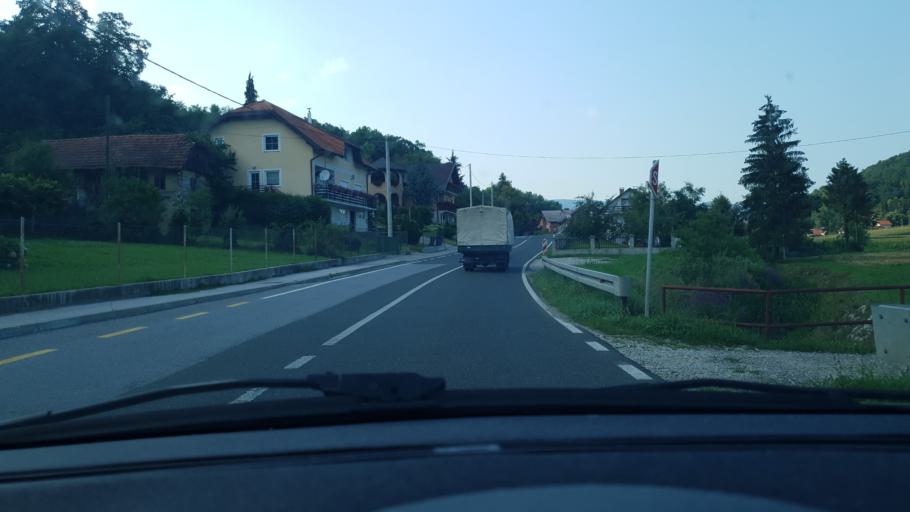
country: HR
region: Krapinsko-Zagorska
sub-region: Grad Krapina
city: Krapina
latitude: 46.1019
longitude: 15.9056
